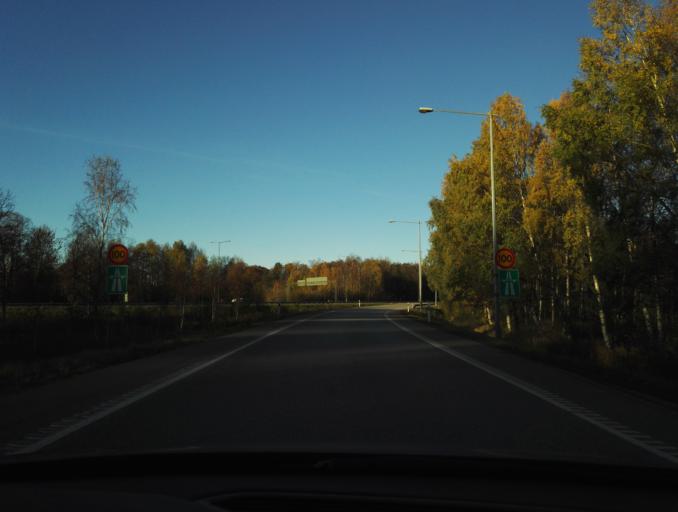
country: SE
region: Kronoberg
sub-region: Vaxjo Kommun
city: Vaexjoe
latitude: 56.8912
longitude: 14.7535
